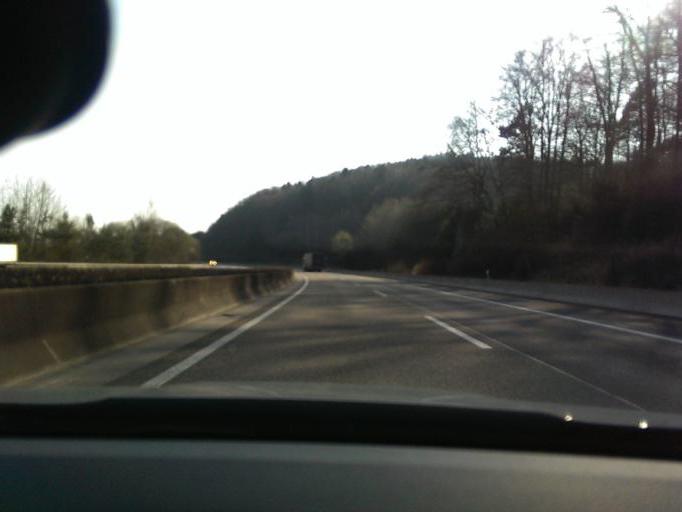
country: DE
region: Thuringia
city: Gerstungen
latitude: 51.0046
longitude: 10.0940
